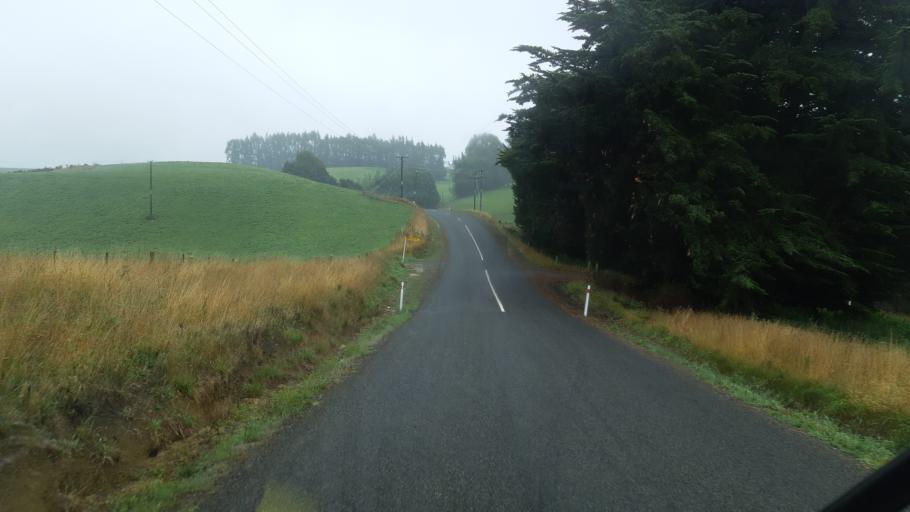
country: NZ
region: Otago
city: Oamaru
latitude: -44.9401
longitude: 170.7570
